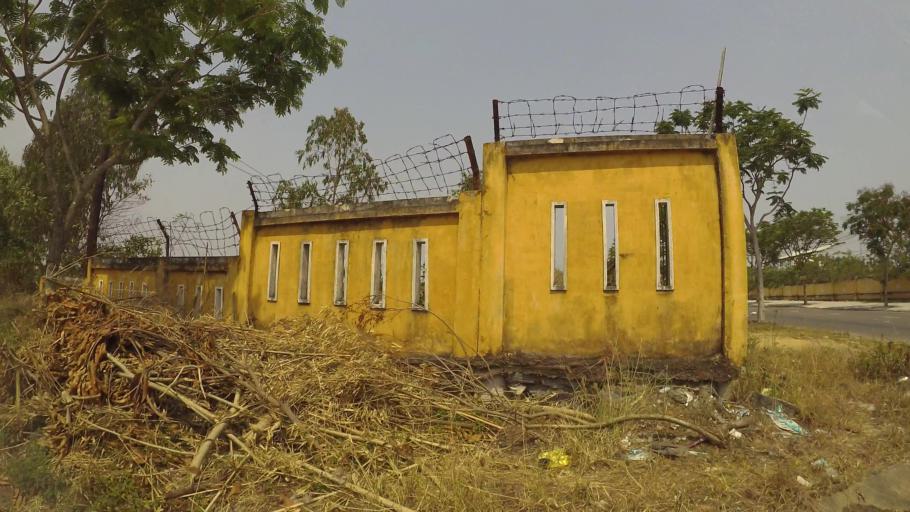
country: VN
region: Da Nang
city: Ngu Hanh Son
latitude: 16.0161
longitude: 108.2511
